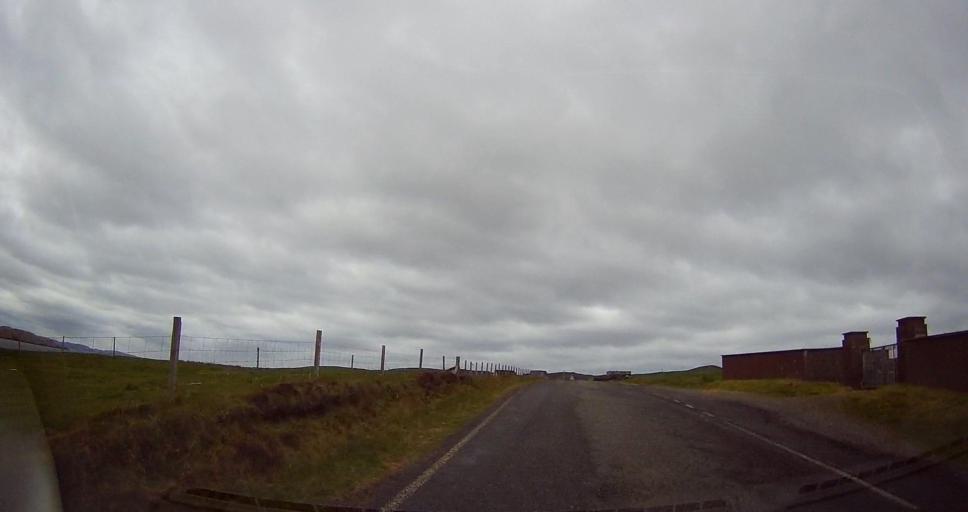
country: GB
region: Scotland
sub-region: Shetland Islands
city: Lerwick
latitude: 60.4819
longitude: -1.4757
